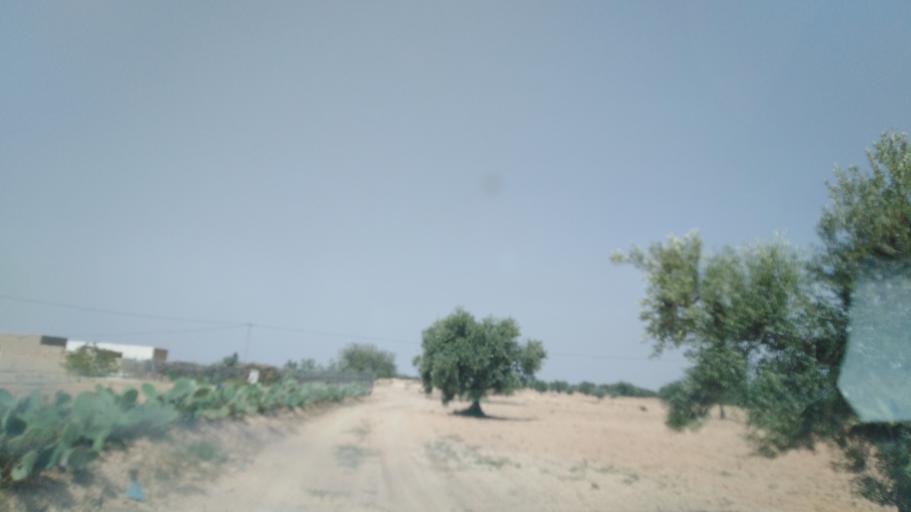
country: TN
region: Safaqis
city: Sfax
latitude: 34.6556
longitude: 10.5548
